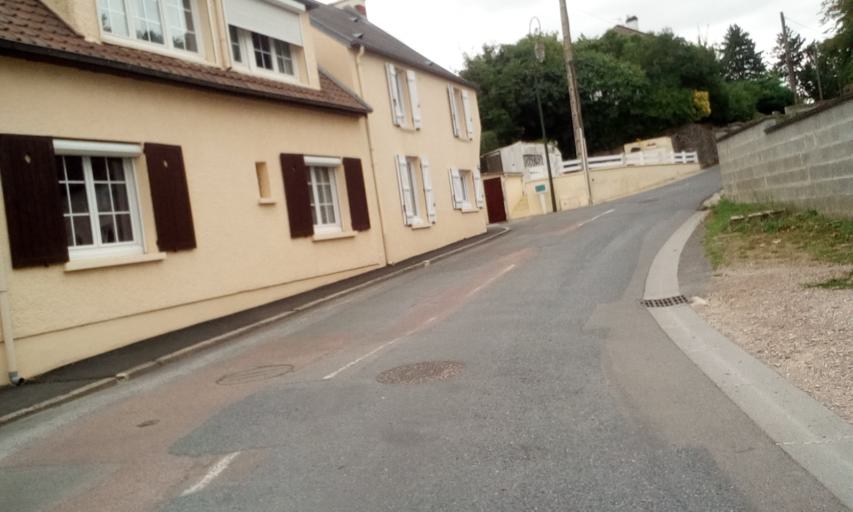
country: FR
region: Lower Normandy
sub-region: Departement du Calvados
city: Eterville
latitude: 49.1574
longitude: -0.4345
